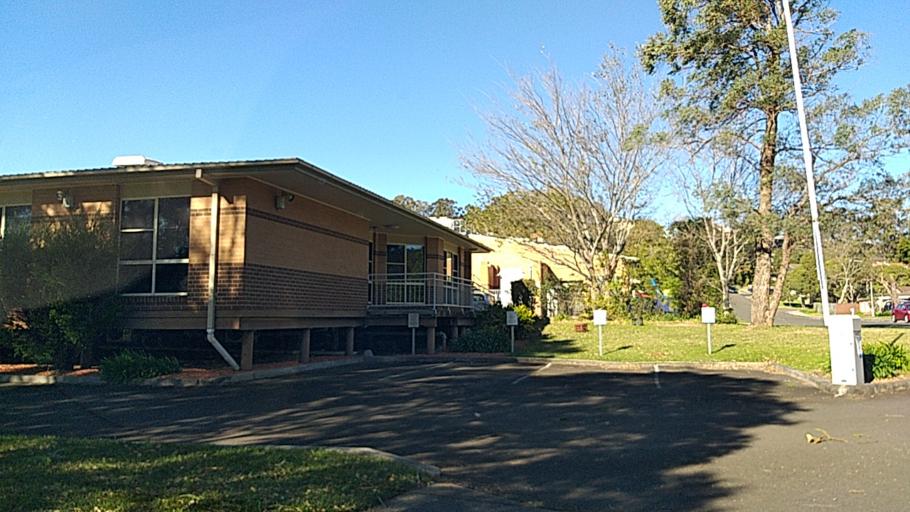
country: AU
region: New South Wales
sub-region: Wollongong
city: Cordeaux Heights
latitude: -34.4389
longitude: 150.8507
